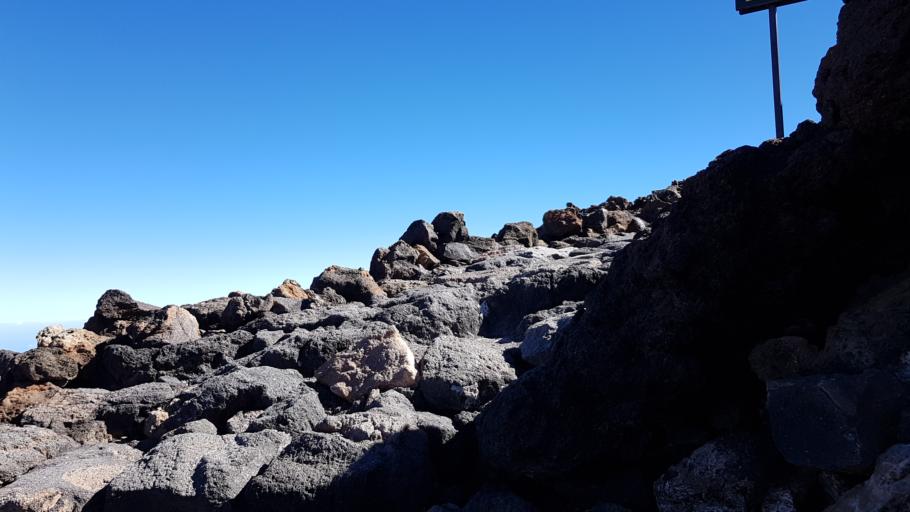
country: ES
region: Canary Islands
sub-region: Provincia de Santa Cruz de Tenerife
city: La Guancha
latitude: 28.2736
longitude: -16.6389
